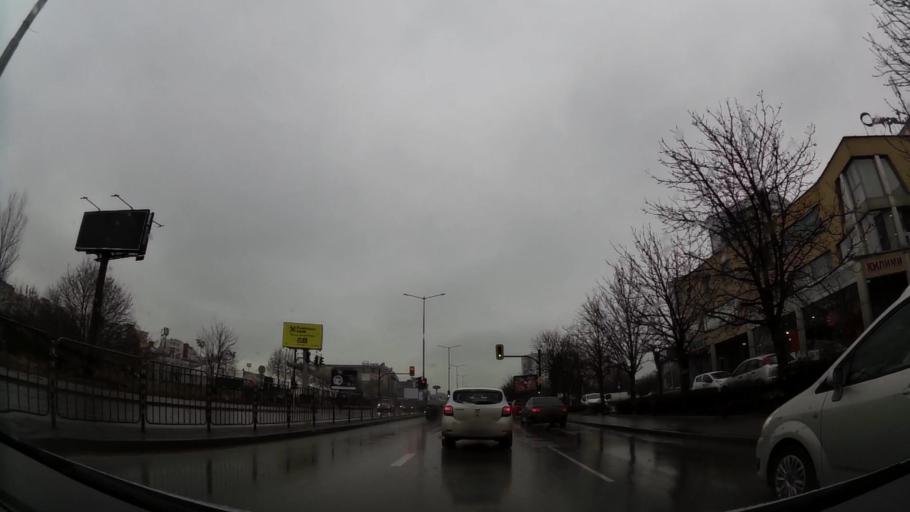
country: BG
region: Sofia-Capital
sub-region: Stolichna Obshtina
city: Sofia
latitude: 42.6539
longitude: 23.3806
